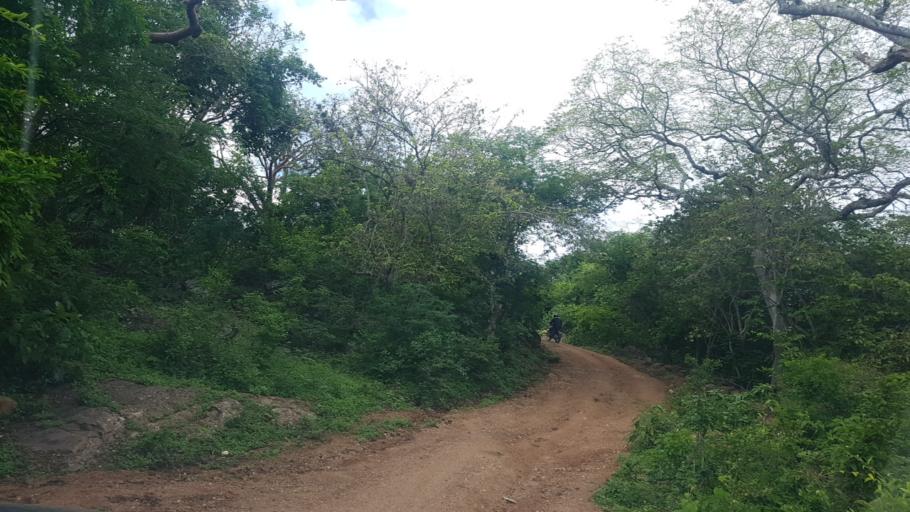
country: NI
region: Nueva Segovia
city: Ocotal
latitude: 13.6365
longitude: -86.6028
